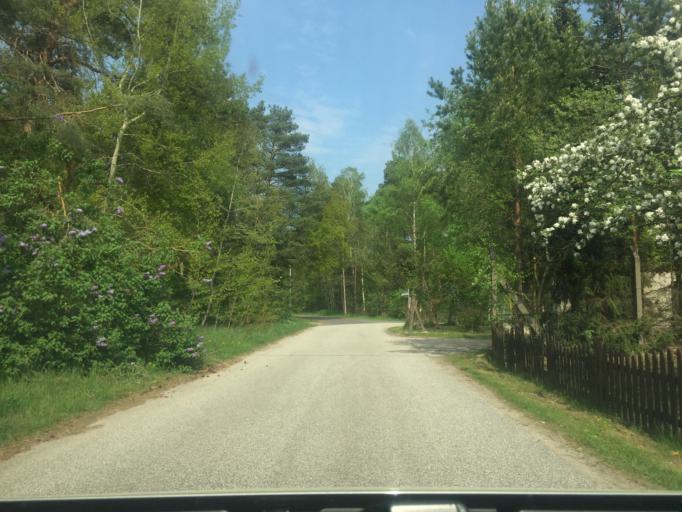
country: DE
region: Mecklenburg-Vorpommern
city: Torgelow
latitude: 53.6157
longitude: 14.0385
